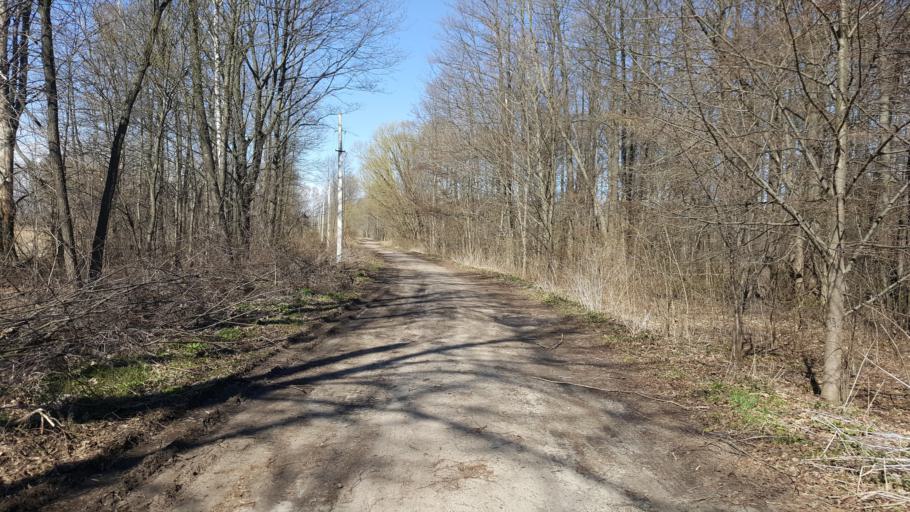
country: BY
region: Brest
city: Zhabinka
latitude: 52.2521
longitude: 23.9494
